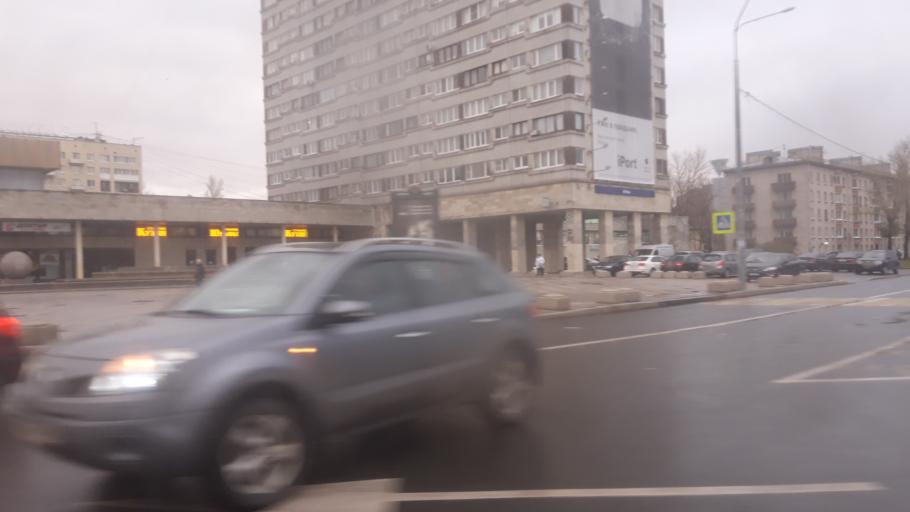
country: RU
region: St.-Petersburg
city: Kupchino
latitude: 59.8442
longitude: 30.3227
